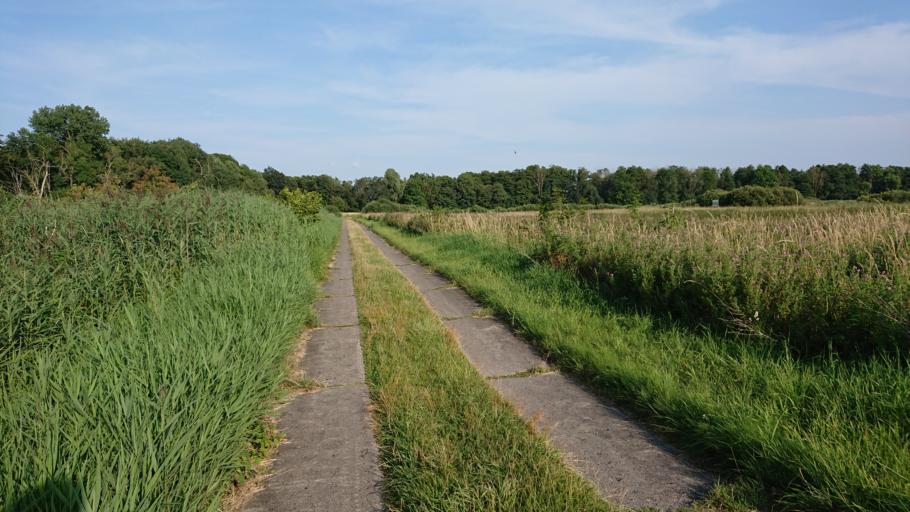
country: DE
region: Mecklenburg-Vorpommern
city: Gormin
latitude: 53.9726
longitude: 13.2969
